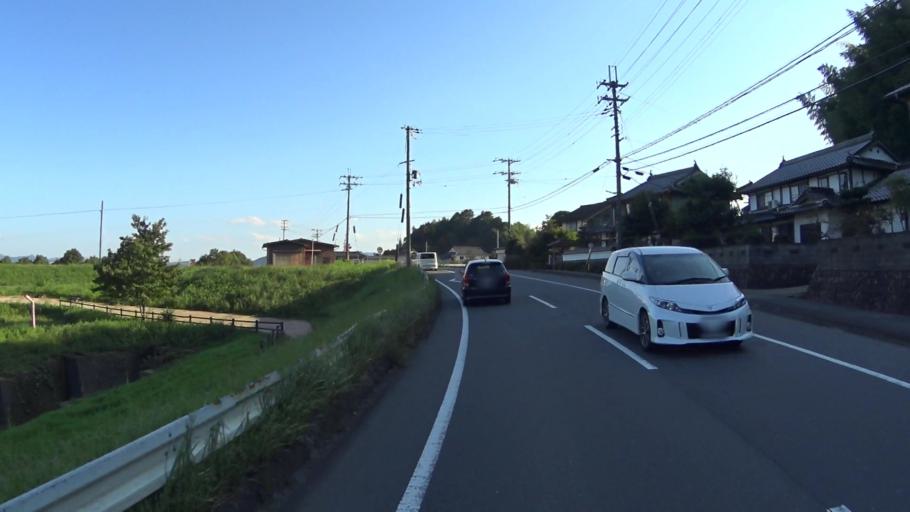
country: JP
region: Kyoto
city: Fukuchiyama
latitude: 35.3146
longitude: 135.1093
